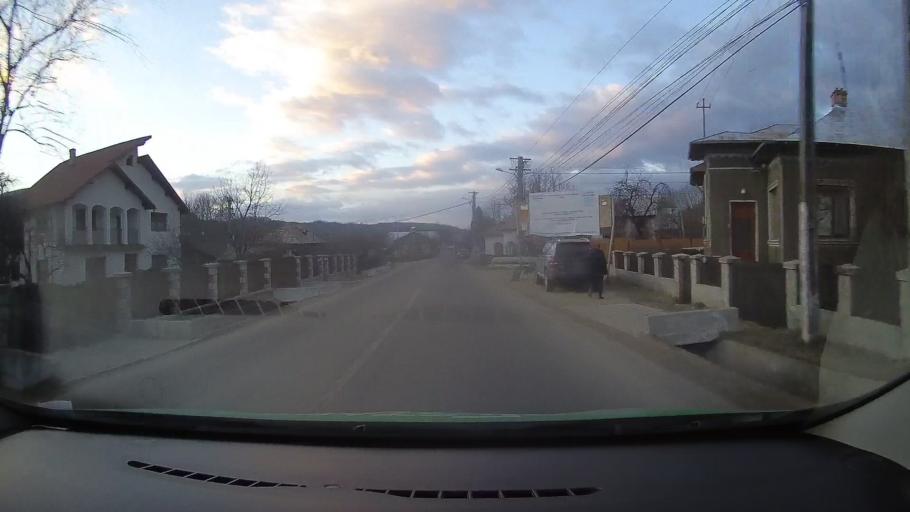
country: RO
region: Dambovita
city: Iedera de Jos
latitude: 45.0202
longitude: 25.6377
